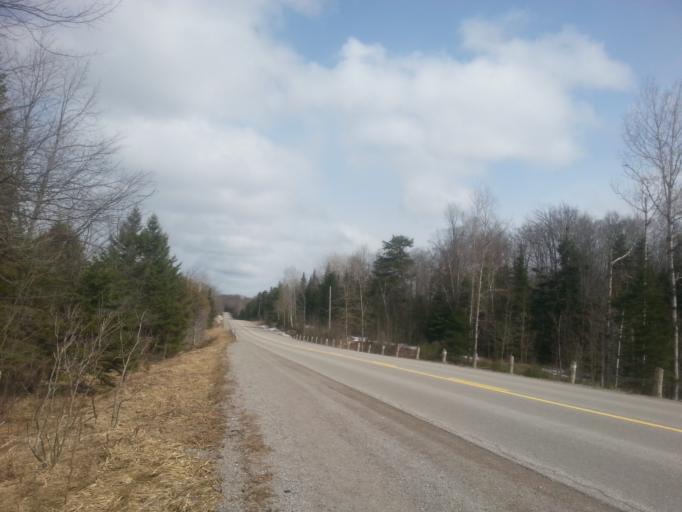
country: CA
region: Ontario
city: Omemee
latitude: 44.7433
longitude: -78.7796
